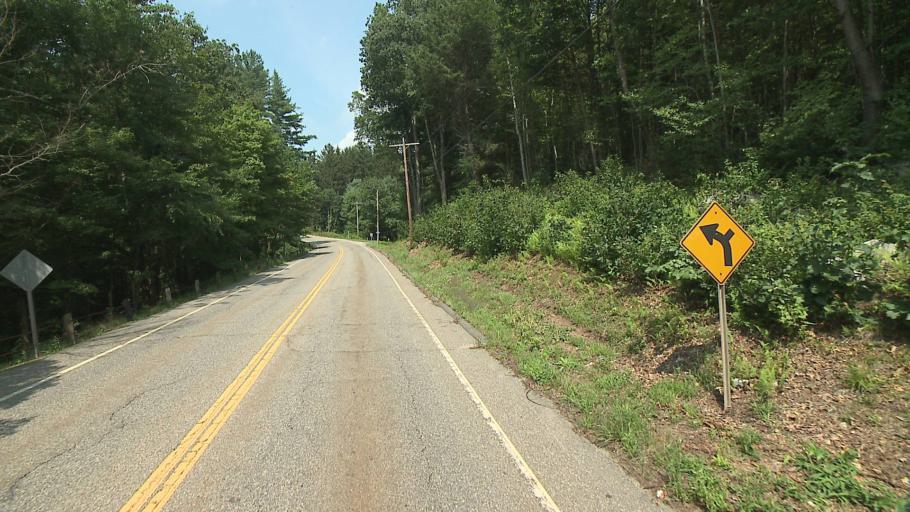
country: US
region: Connecticut
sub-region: Litchfield County
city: Bethlehem Village
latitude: 41.6735
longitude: -73.1489
